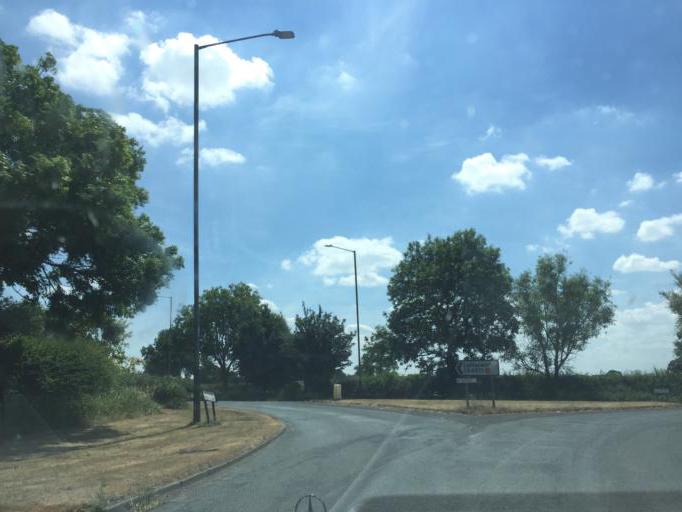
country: GB
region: England
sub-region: Leicestershire
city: Hinckley
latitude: 52.4964
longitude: -1.3575
